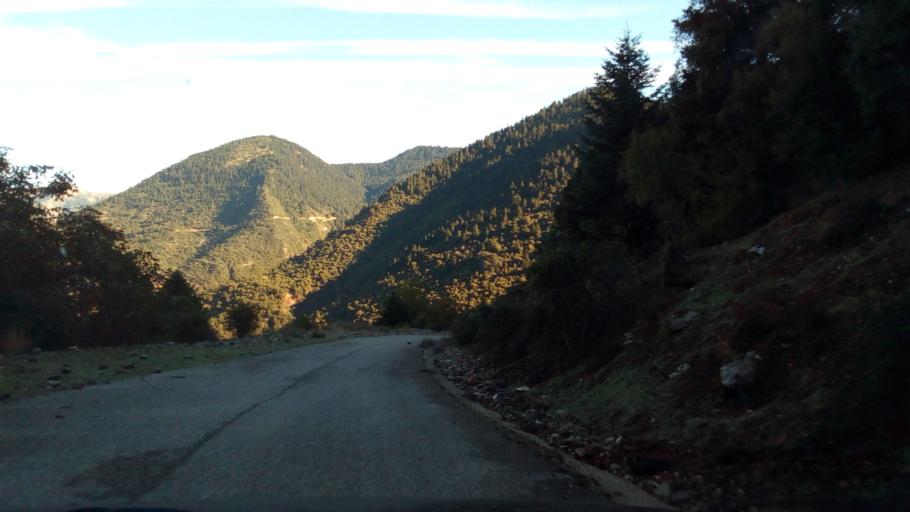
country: GR
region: West Greece
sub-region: Nomos Aitolias kai Akarnanias
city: Nafpaktos
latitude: 38.5514
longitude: 21.8535
